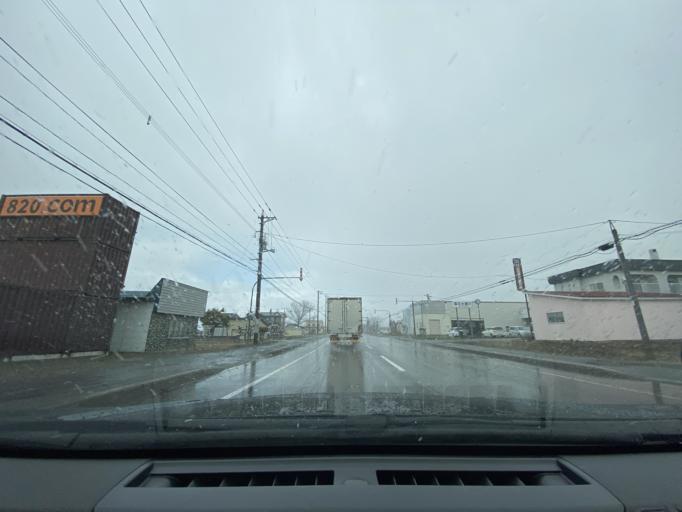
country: JP
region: Hokkaido
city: Takikawa
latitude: 43.6314
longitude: 141.9440
